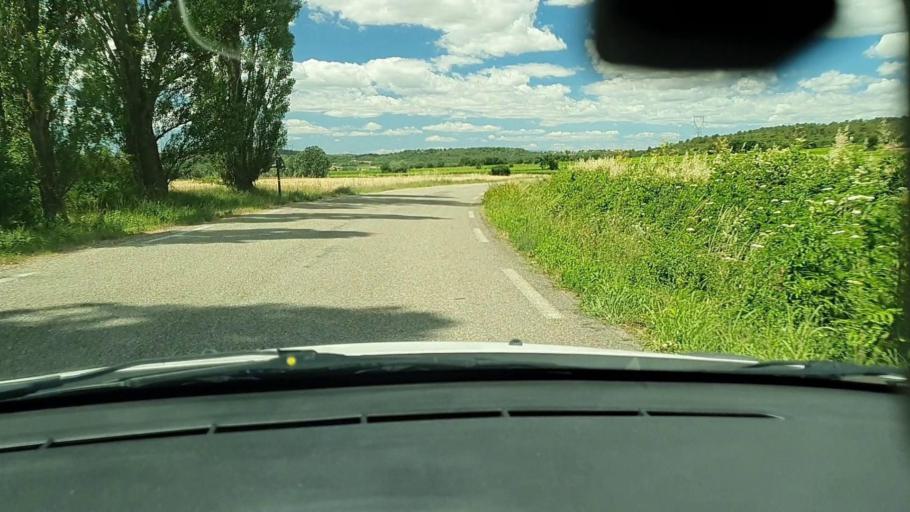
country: FR
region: Languedoc-Roussillon
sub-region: Departement du Gard
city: Blauzac
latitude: 43.9522
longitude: 4.4094
